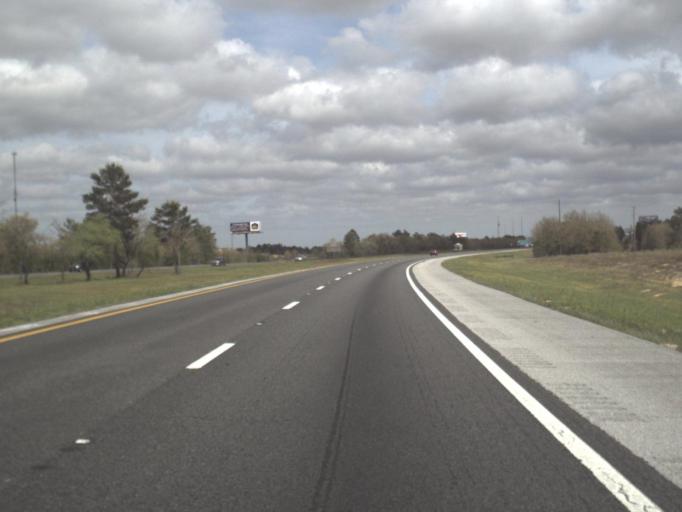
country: US
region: Florida
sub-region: Okaloosa County
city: Crestview
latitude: 30.7336
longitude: -86.3717
